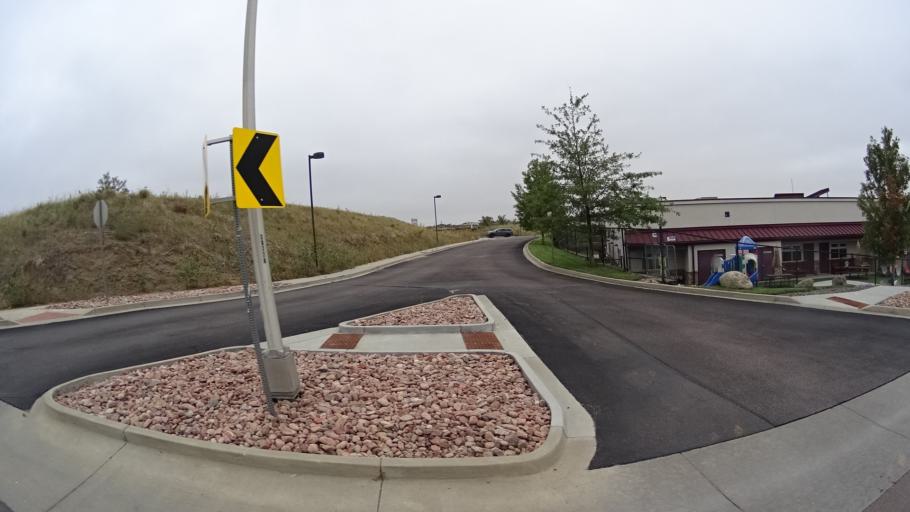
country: US
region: Colorado
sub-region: El Paso County
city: Cimarron Hills
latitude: 38.9061
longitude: -104.7178
